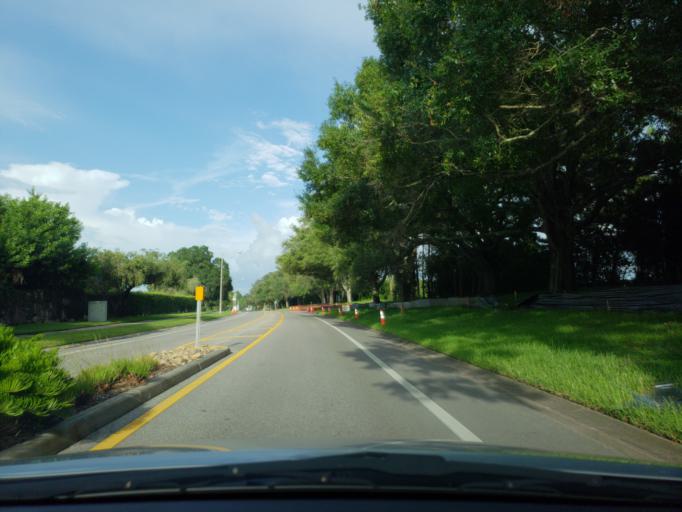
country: US
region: Florida
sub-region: Hillsborough County
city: Carrollwood Village
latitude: 28.0732
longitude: -82.5263
